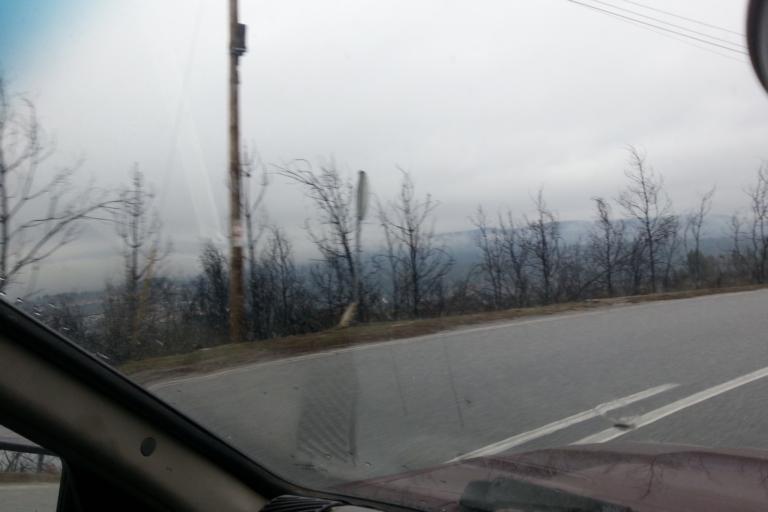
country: PT
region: Viseu
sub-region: Mangualde
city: Mangualde
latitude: 40.6099
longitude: -7.7021
